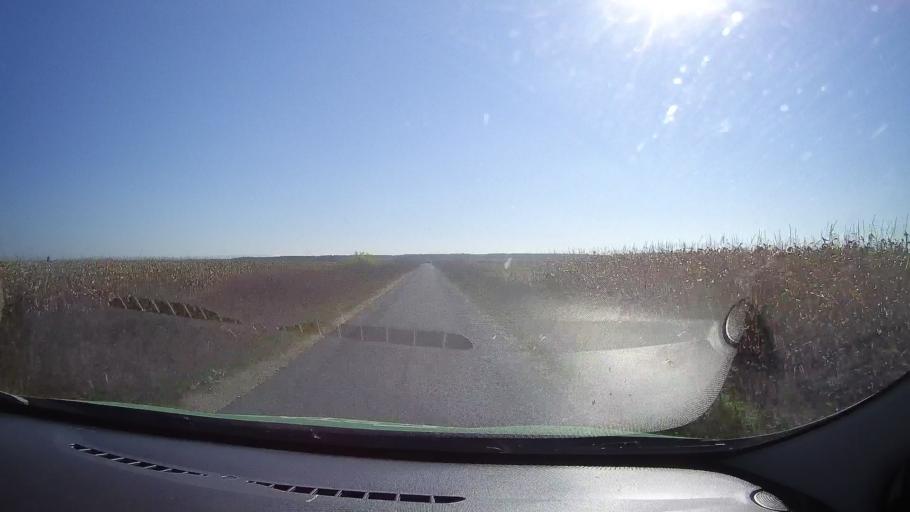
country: RO
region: Satu Mare
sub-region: Comuna Doba
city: Doba
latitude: 47.7340
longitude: 22.7223
